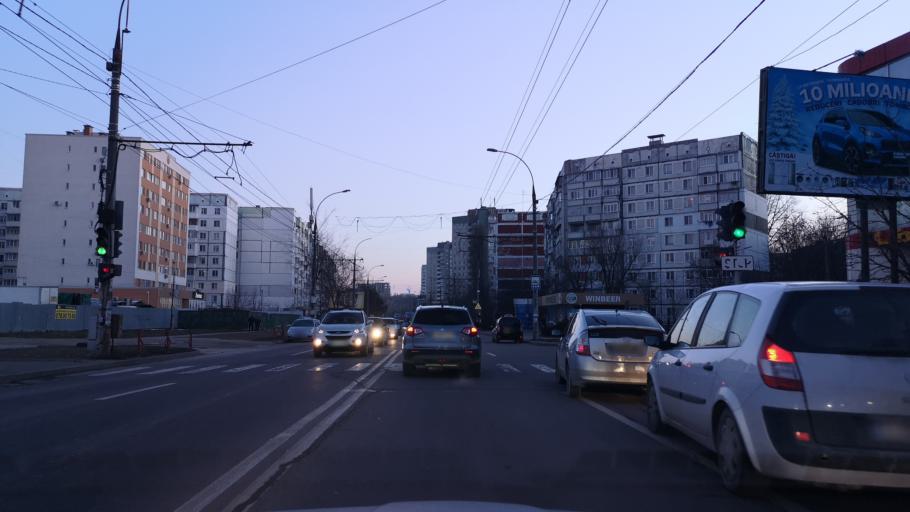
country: MD
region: Chisinau
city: Stauceni
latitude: 47.0581
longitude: 28.8476
